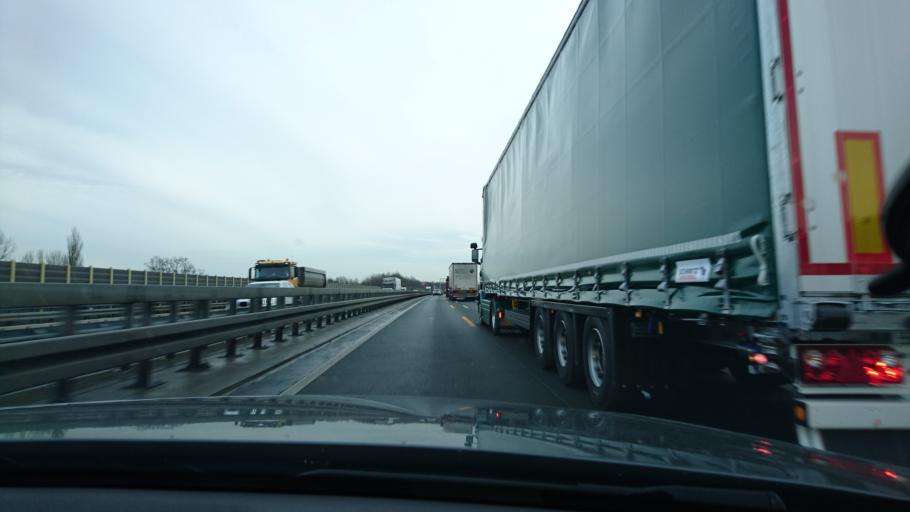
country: DE
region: North Rhine-Westphalia
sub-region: Regierungsbezirk Munster
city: Lotte
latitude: 52.2962
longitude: 7.9417
